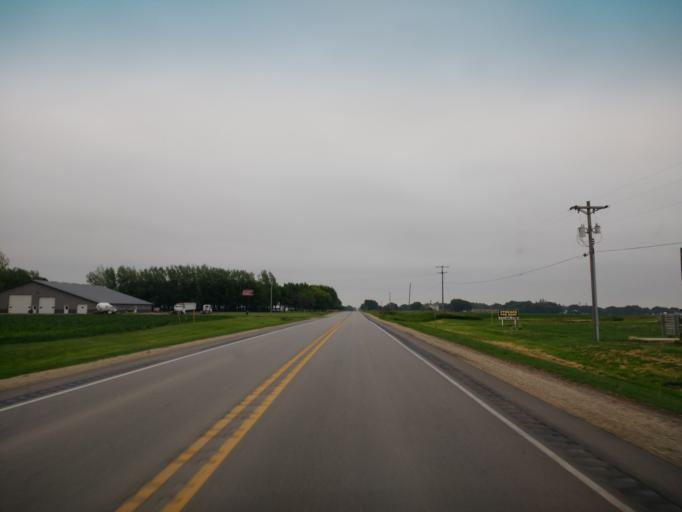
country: US
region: Iowa
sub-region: O'Brien County
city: Hartley
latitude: 43.1849
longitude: -95.5001
